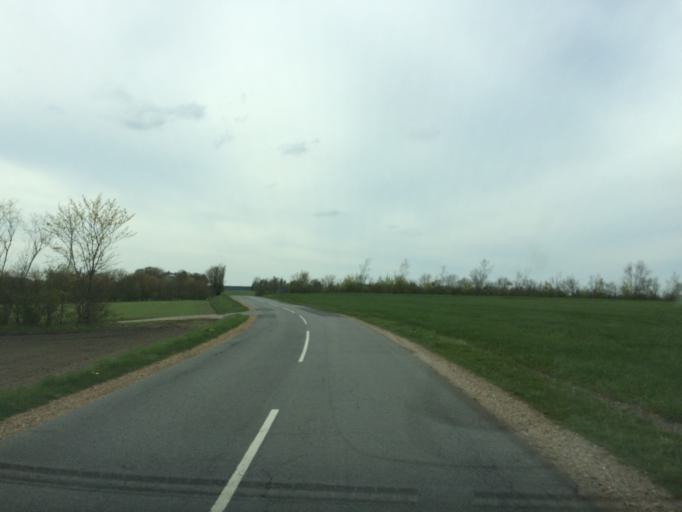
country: DK
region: Central Jutland
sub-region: Ringkobing-Skjern Kommune
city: Videbaek
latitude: 56.2034
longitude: 8.5091
